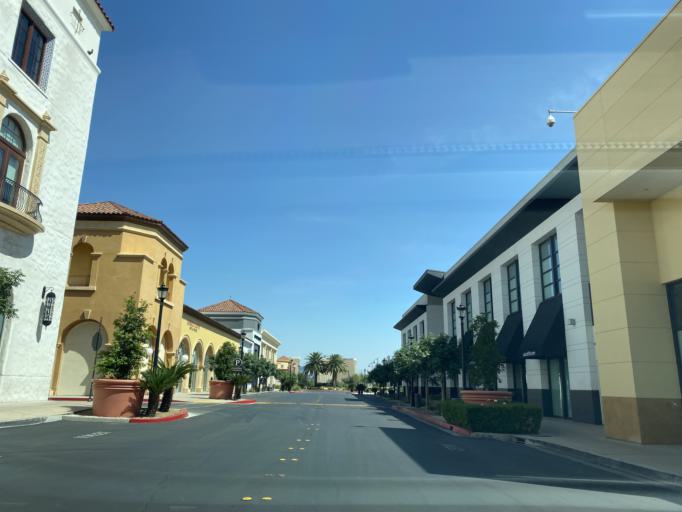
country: US
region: Nevada
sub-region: Clark County
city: Paradise
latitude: 36.0686
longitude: -115.1750
